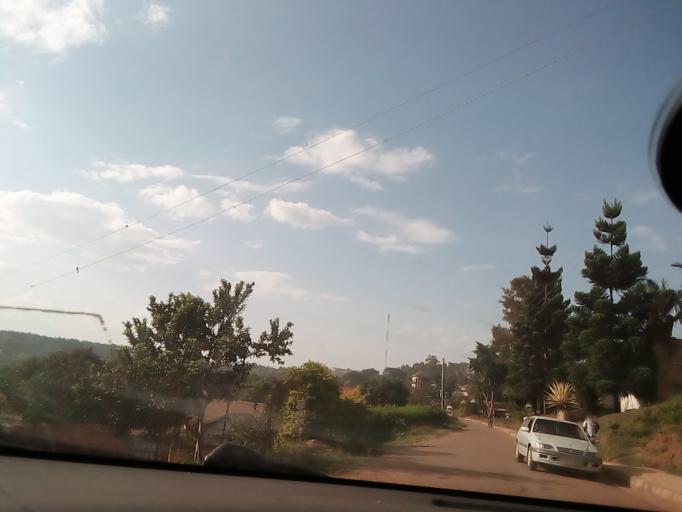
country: UG
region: Central Region
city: Masaka
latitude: -0.3528
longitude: 31.7435
